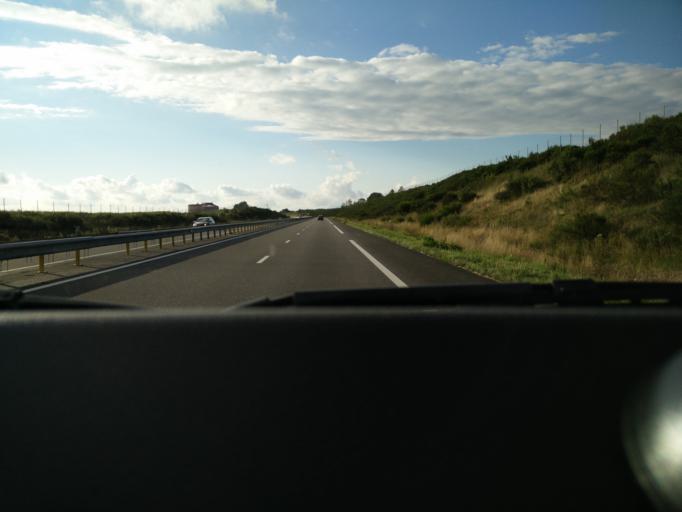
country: FR
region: Lorraine
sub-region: Departement de Meurthe-et-Moselle
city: Baccarat
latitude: 48.5221
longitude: 6.6420
